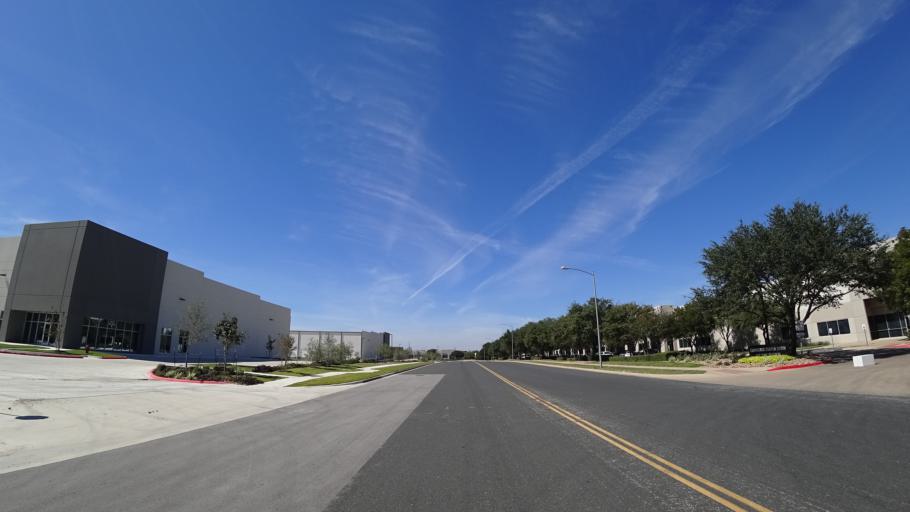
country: US
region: Texas
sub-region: Travis County
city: Austin
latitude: 30.2098
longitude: -97.7178
